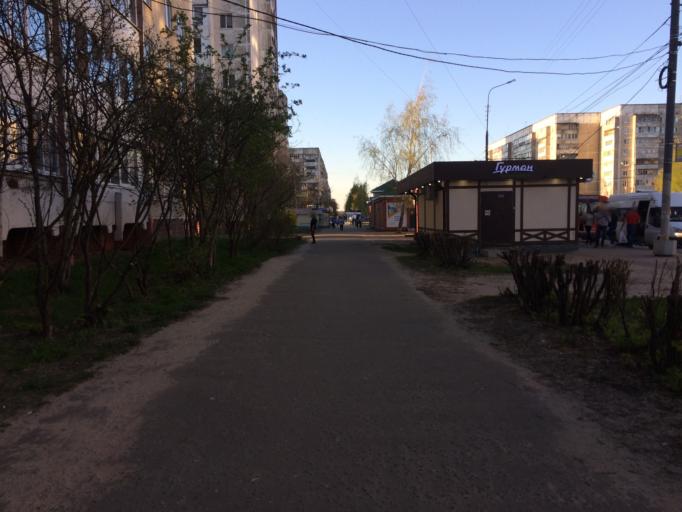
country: RU
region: Mariy-El
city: Yoshkar-Ola
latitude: 56.6297
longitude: 47.9168
